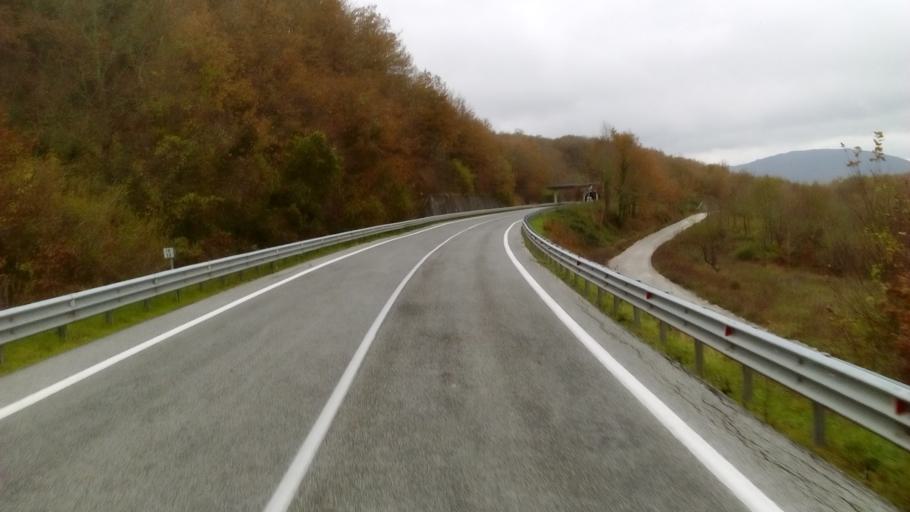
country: IT
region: Molise
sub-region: Provincia di Isernia
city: Chiauci
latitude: 41.6719
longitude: 14.3632
